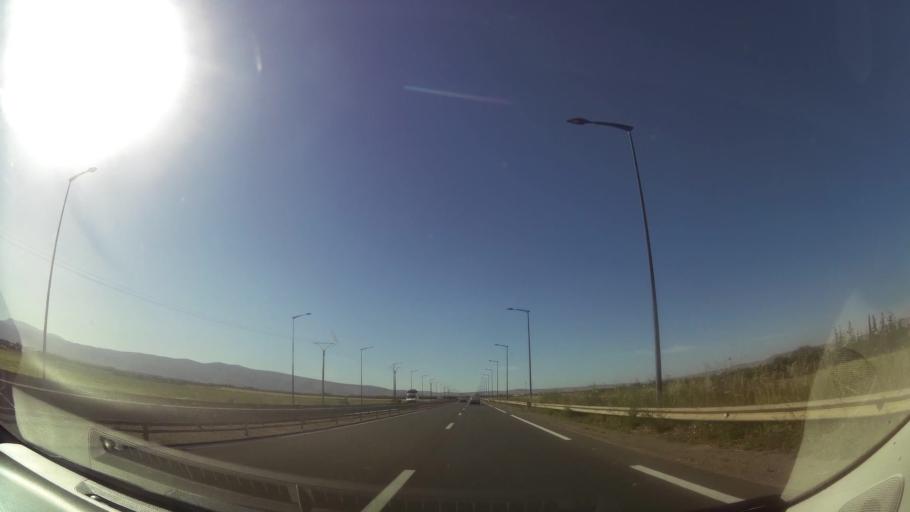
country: MA
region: Oriental
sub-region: Oujda-Angad
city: Oujda
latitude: 34.8322
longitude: -1.9756
